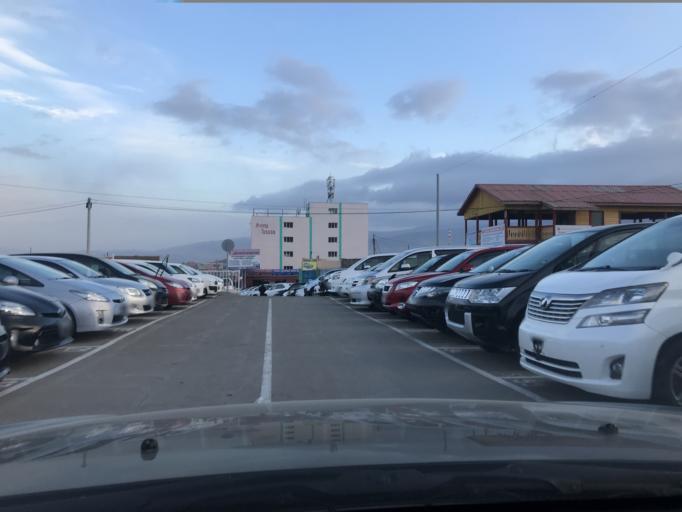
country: MN
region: Ulaanbaatar
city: Ulaanbaatar
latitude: 47.9299
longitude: 107.0017
